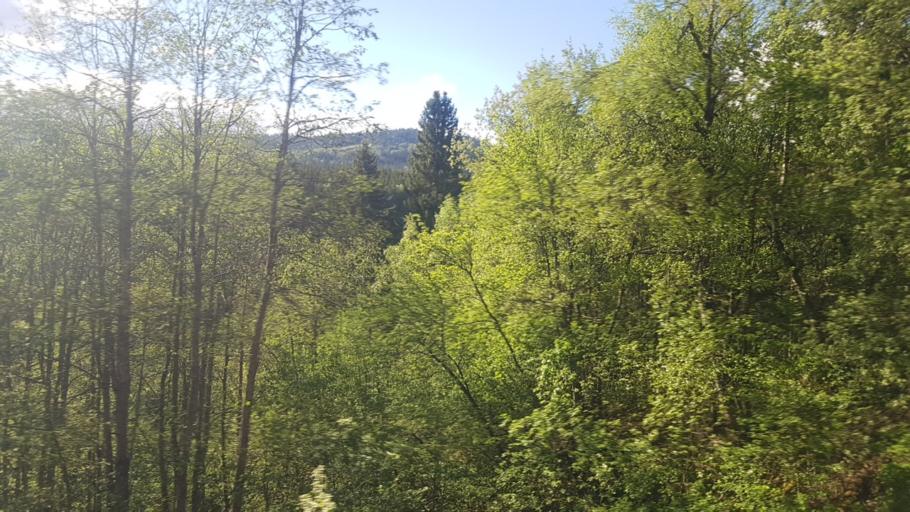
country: NO
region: Sor-Trondelag
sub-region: Midtre Gauldal
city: Storen
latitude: 62.9720
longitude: 10.2086
